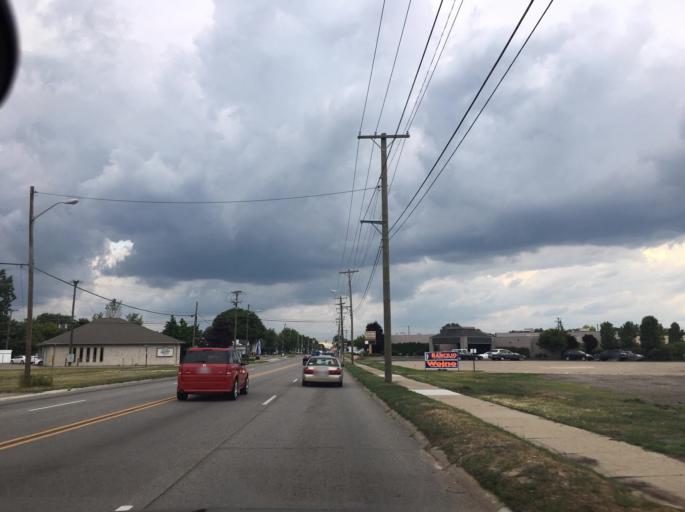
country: US
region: Michigan
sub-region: Macomb County
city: Fraser
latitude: 42.5292
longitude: -82.9471
